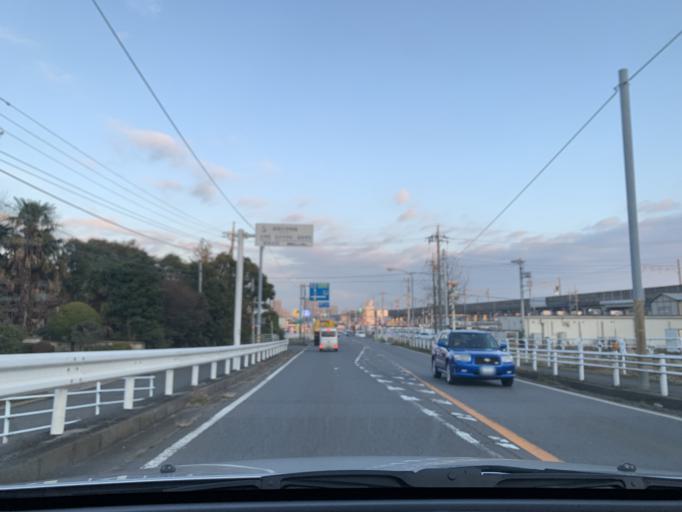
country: JP
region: Chiba
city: Matsudo
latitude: 35.7644
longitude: 139.9181
